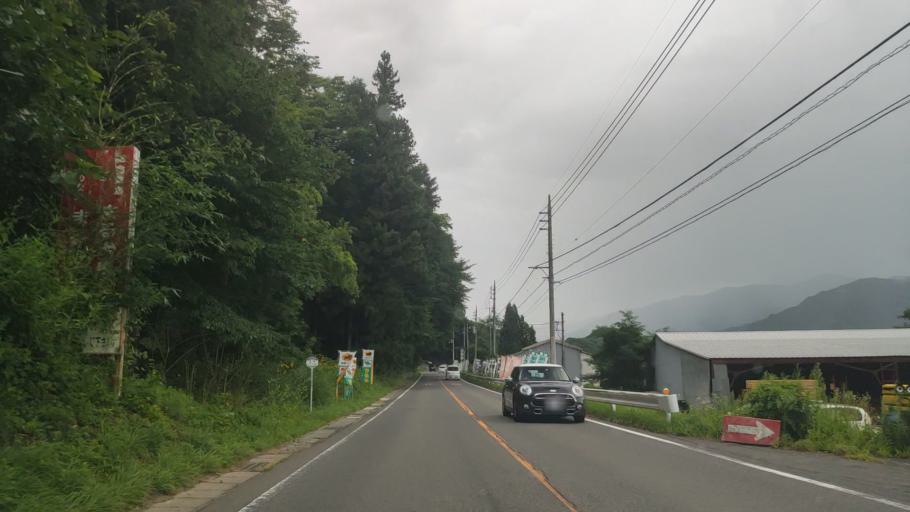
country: JP
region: Gunma
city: Numata
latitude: 36.7157
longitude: 139.2112
